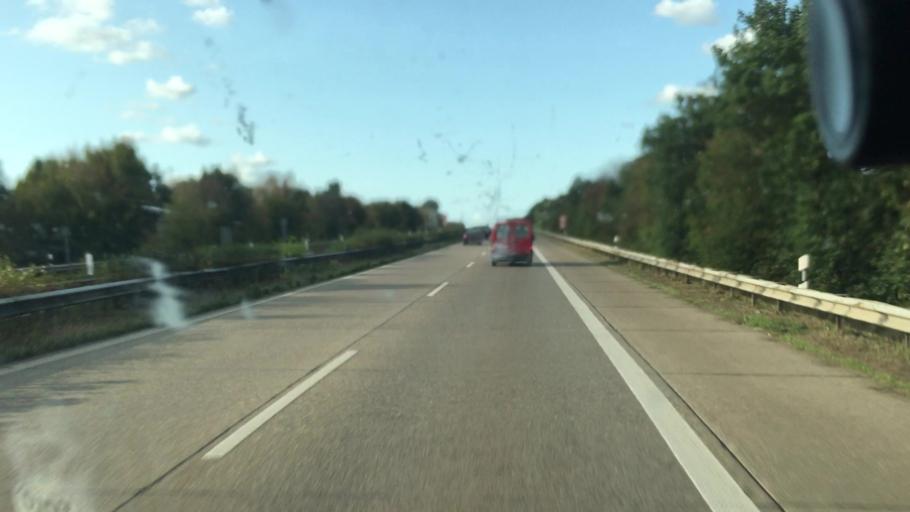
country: DE
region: Lower Saxony
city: Oldenburg
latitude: 53.1450
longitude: 8.2760
